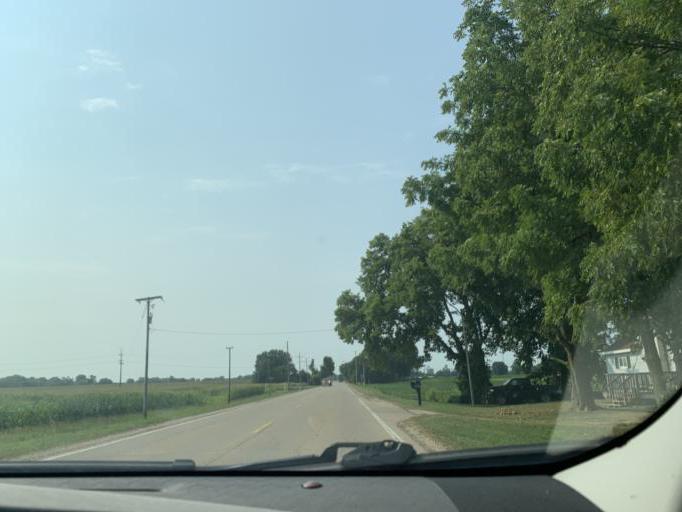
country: US
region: Illinois
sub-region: Whiteside County
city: Sterling
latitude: 41.8031
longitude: -89.7421
